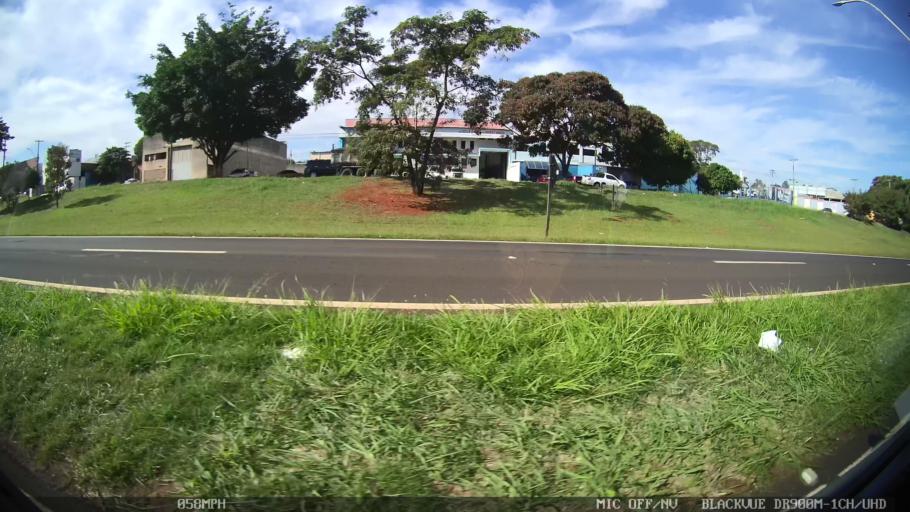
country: BR
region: Sao Paulo
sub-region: Araraquara
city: Araraquara
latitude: -21.8225
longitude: -48.1558
